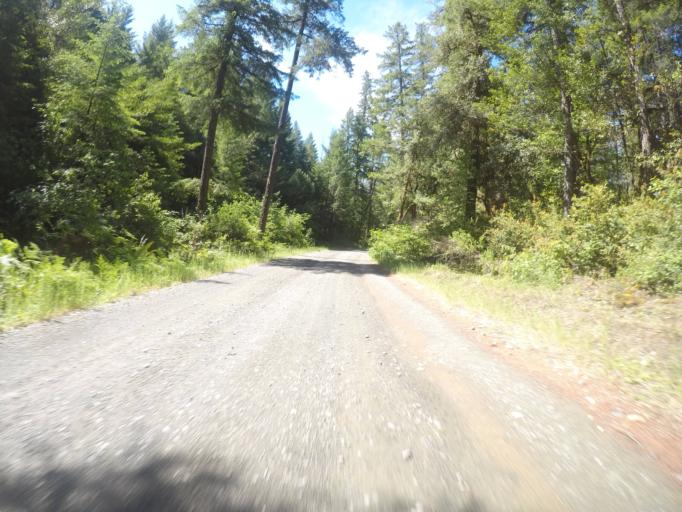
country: US
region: California
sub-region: Del Norte County
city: Bertsch-Oceanview
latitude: 41.6939
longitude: -123.9030
